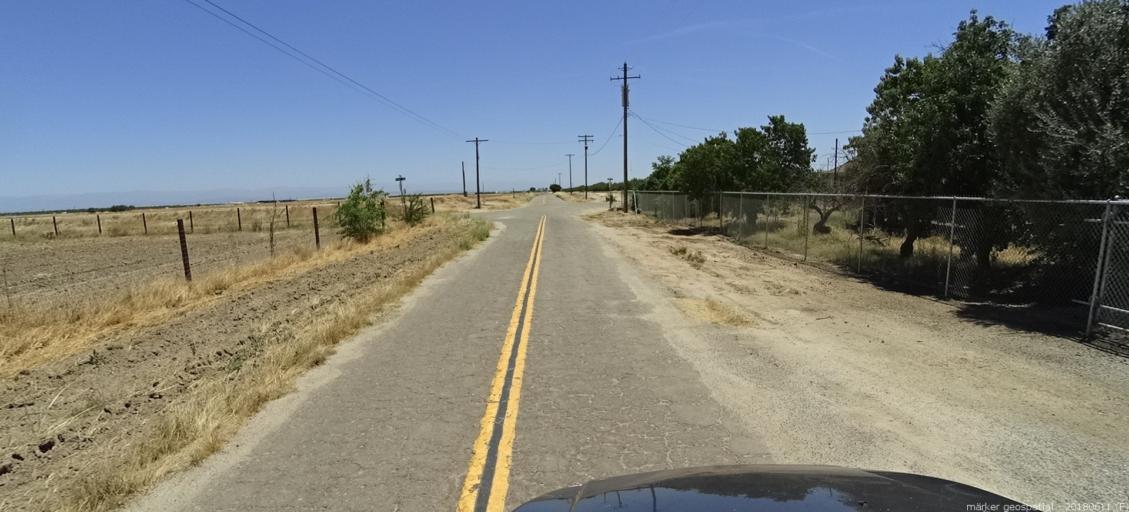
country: US
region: California
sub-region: Madera County
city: Fairmead
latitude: 37.0546
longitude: -120.1849
